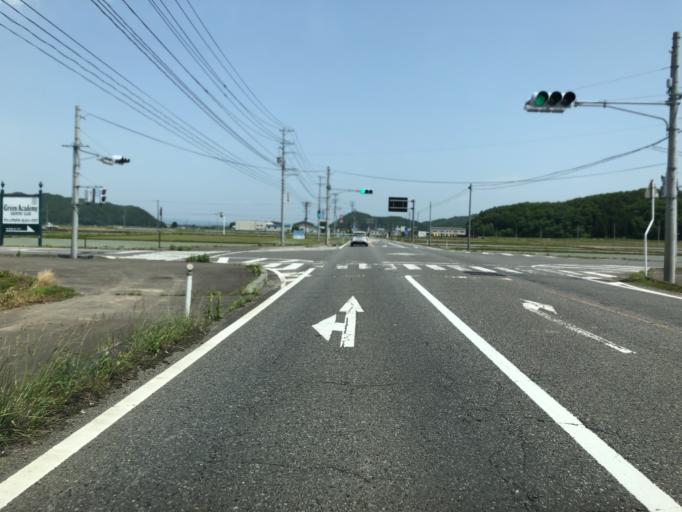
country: JP
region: Fukushima
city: Ishikawa
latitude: 37.1160
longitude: 140.2771
